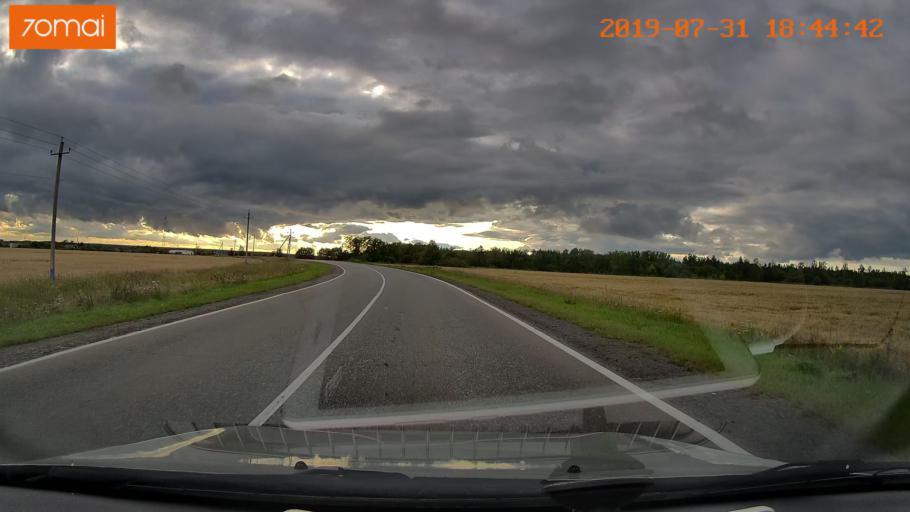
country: RU
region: Moskovskaya
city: Troitskoye
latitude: 55.2516
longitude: 38.5464
